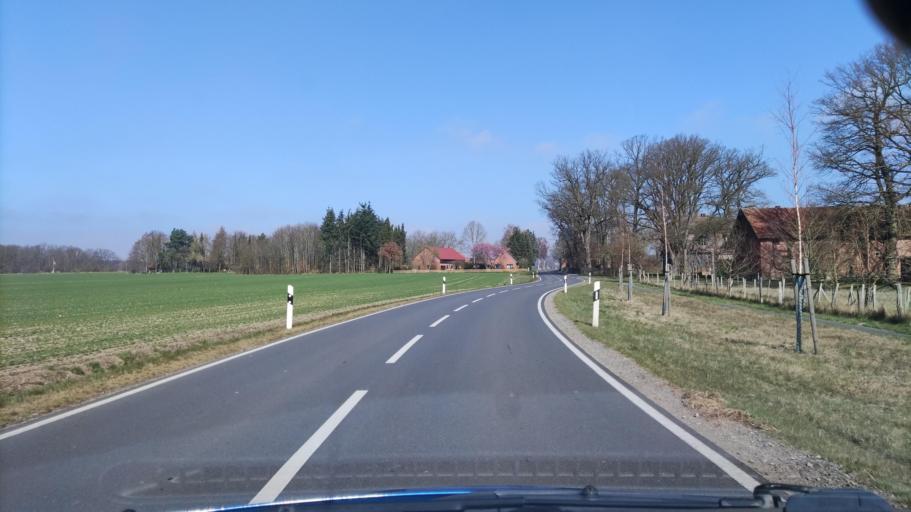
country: DE
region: Lower Saxony
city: Clenze
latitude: 52.9649
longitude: 10.9723
